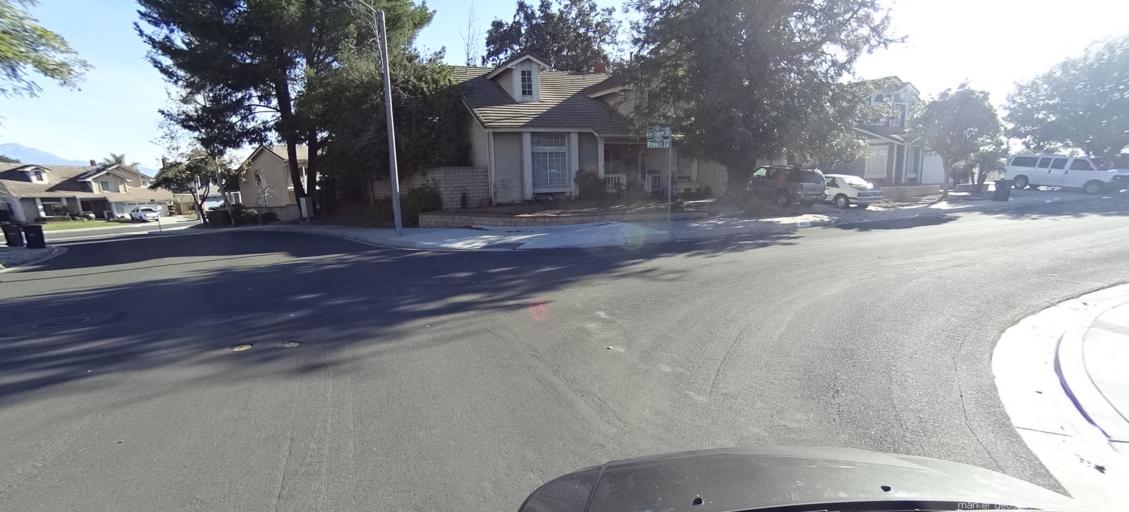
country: US
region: California
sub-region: Los Angeles County
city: Walnut
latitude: 33.9819
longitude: -117.8478
